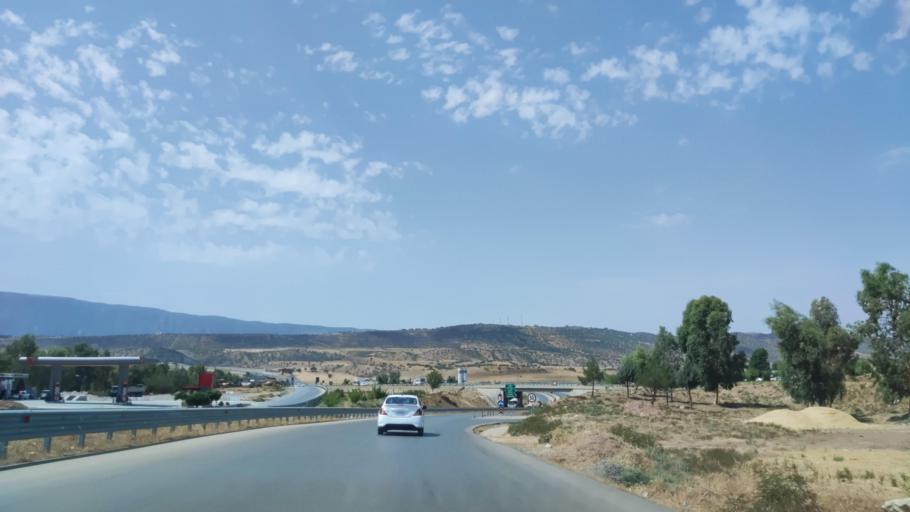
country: IQ
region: Arbil
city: Shaqlawah
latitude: 36.4584
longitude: 44.3864
